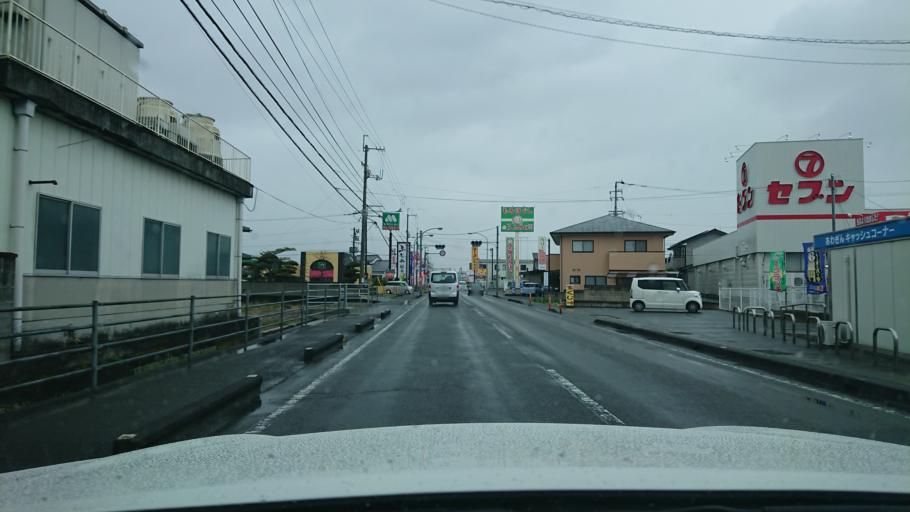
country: JP
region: Tokushima
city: Ishii
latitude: 34.0850
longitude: 134.4811
